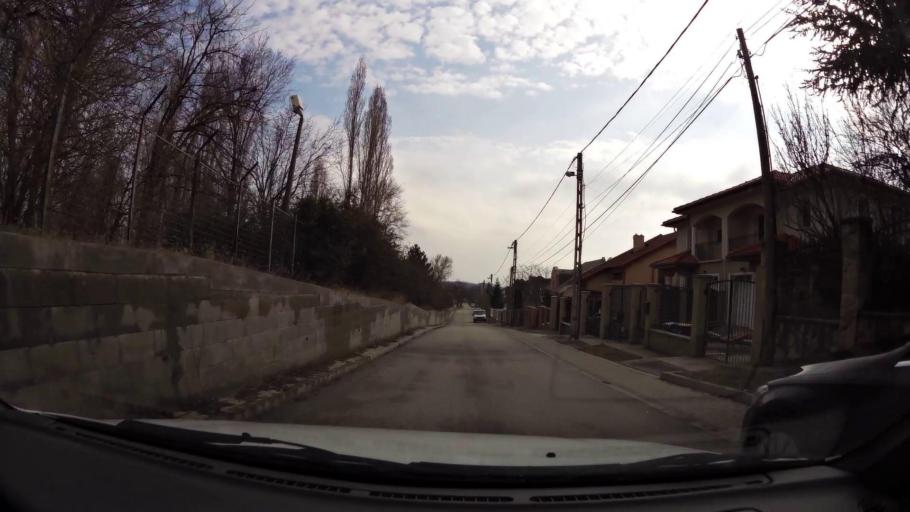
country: HU
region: Pest
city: Csomor
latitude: 47.5208
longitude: 19.2367
